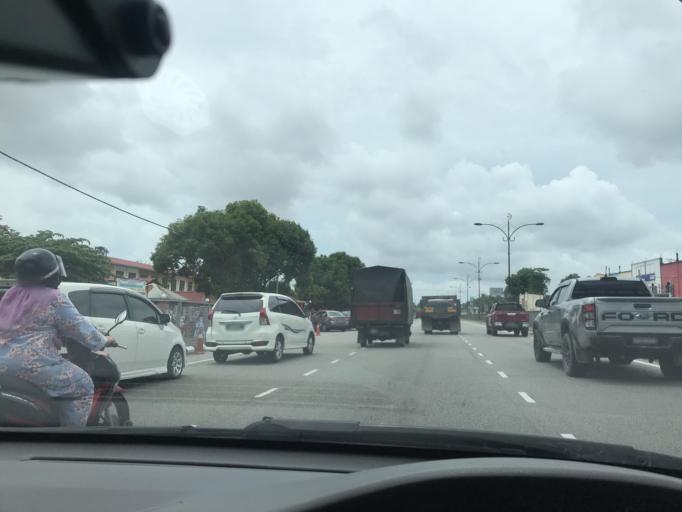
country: MY
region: Kelantan
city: Kota Bharu
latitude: 6.1182
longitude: 102.2201
